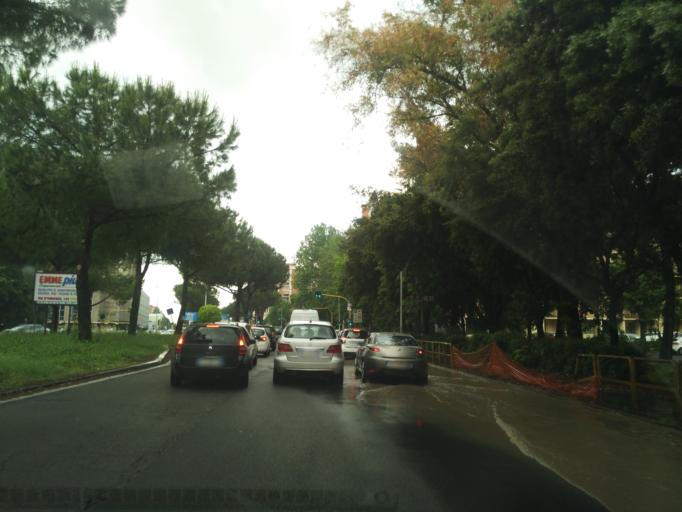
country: IT
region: Latium
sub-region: Citta metropolitana di Roma Capitale
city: Rome
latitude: 41.9094
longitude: 12.5726
